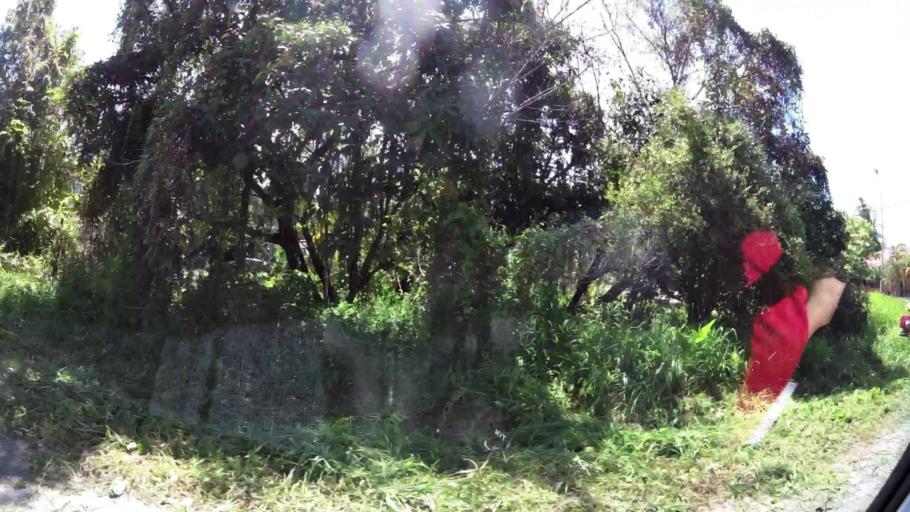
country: BN
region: Brunei and Muara
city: Bandar Seri Begawan
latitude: 4.9411
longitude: 114.9479
